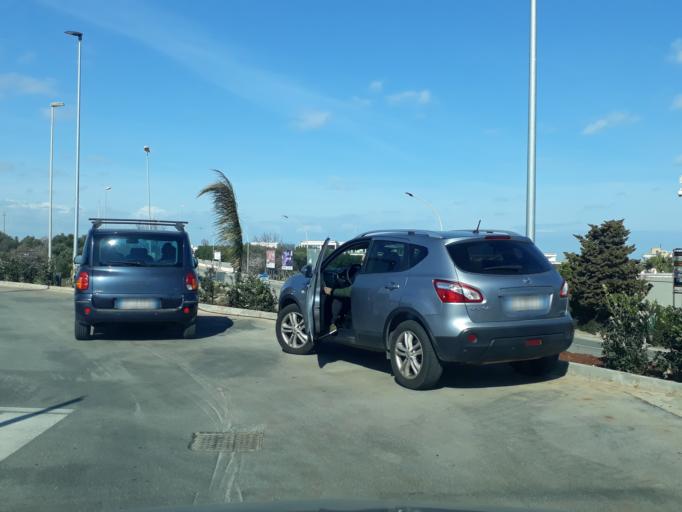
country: IT
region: Apulia
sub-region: Provincia di Bari
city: Monopoli
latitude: 40.9708
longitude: 17.2641
